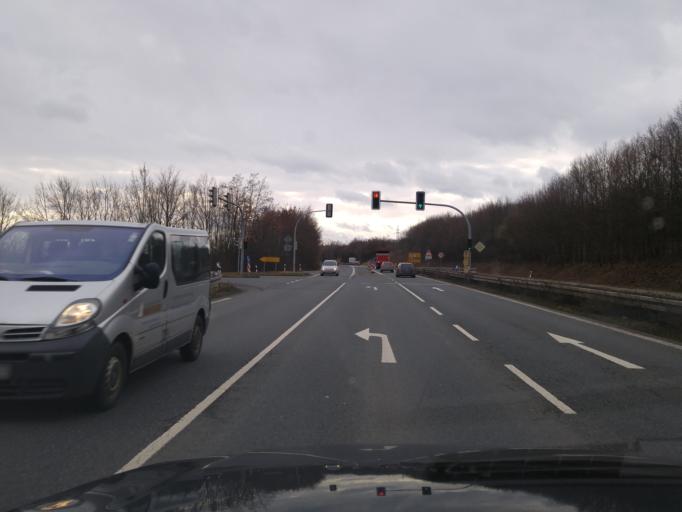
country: DE
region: Saxony
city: Dennheritz
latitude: 50.7964
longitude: 12.4792
